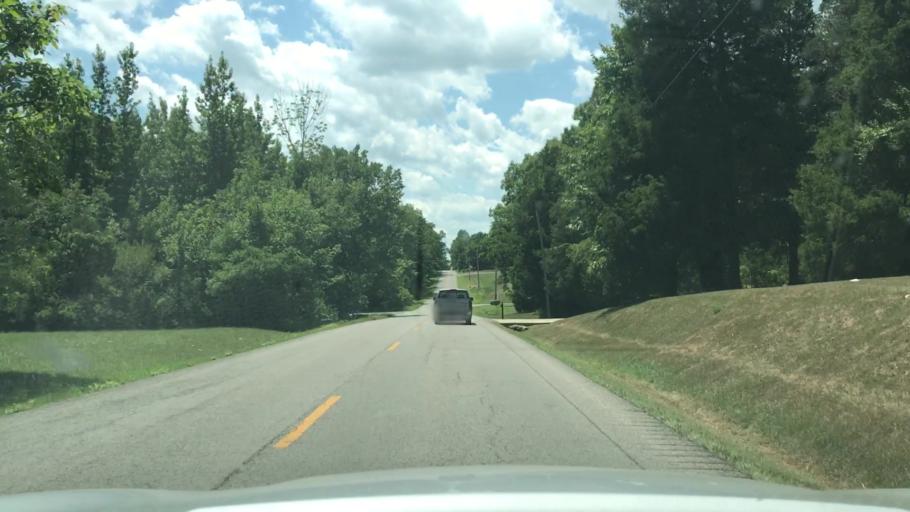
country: US
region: Kentucky
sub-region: Muhlenberg County
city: Greenville
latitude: 37.1852
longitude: -87.2266
